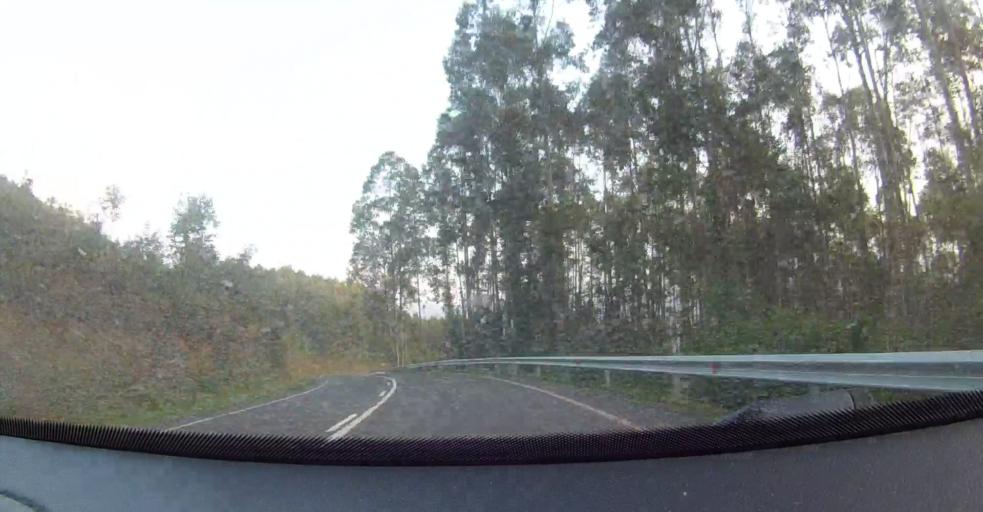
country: ES
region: Basque Country
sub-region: Bizkaia
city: Sopuerta
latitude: 43.2968
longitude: -3.1660
